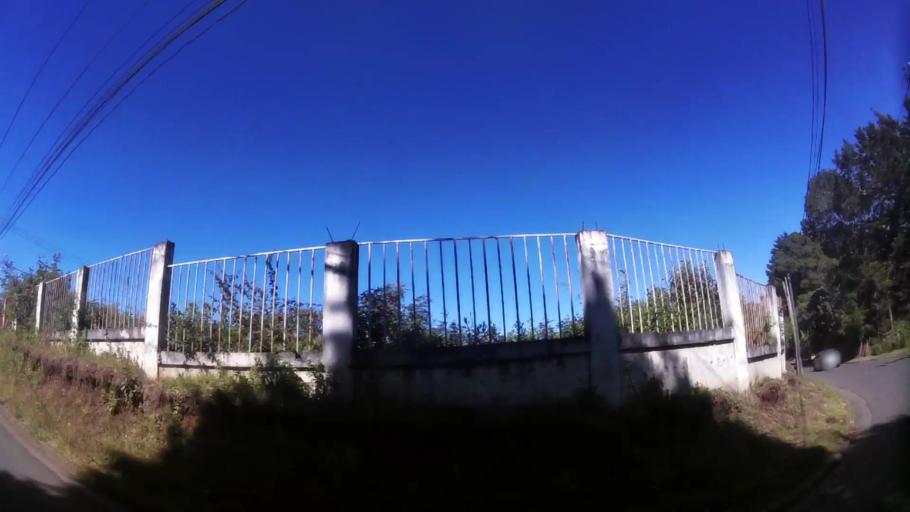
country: GT
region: Guatemala
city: San Jose Pinula
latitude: 14.5105
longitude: -90.4237
